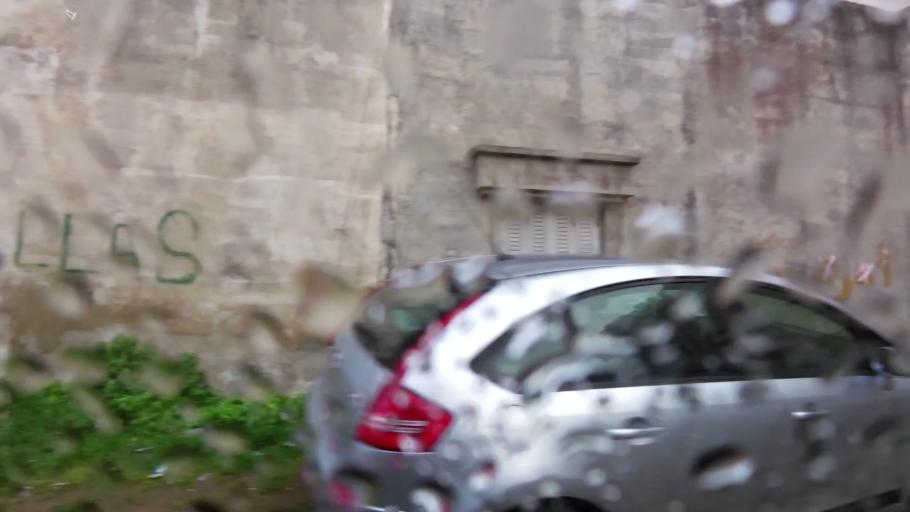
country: MA
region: Doukkala-Abda
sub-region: El-Jadida
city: El Jadida
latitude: 33.2462
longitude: -8.5254
